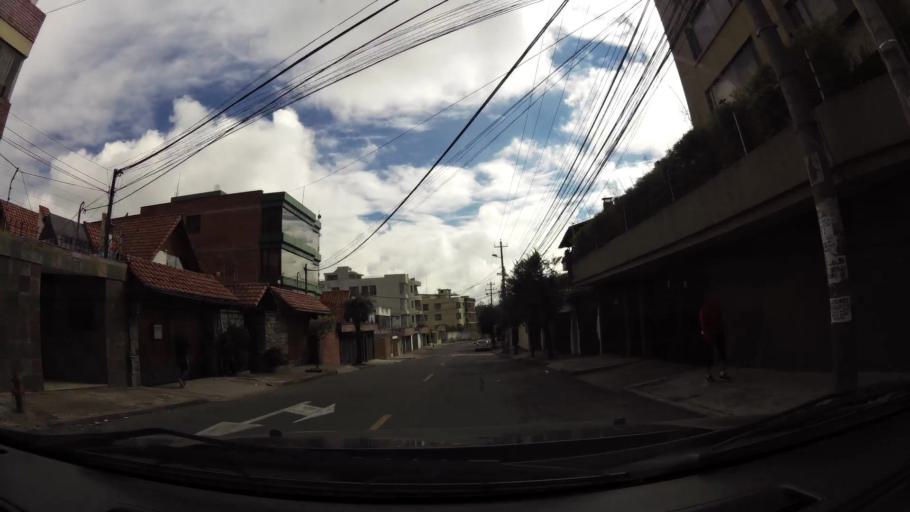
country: EC
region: Pichincha
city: Quito
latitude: -0.1682
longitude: -78.4685
